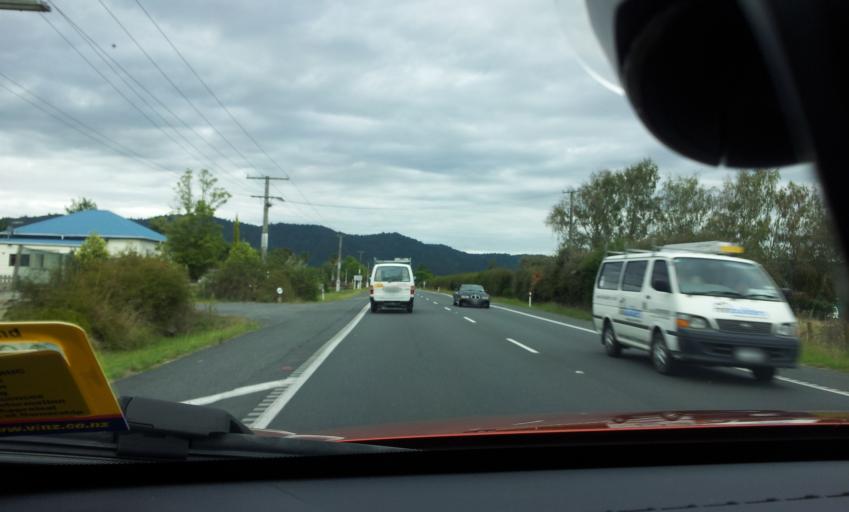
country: NZ
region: Waikato
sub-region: Waikato District
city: Ngaruawahia
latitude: -37.6823
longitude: 175.1687
